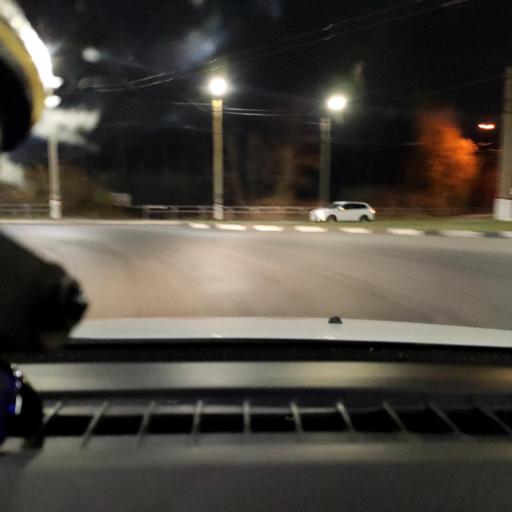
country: RU
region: Samara
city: Novokuybyshevsk
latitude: 53.1026
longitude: 49.9393
